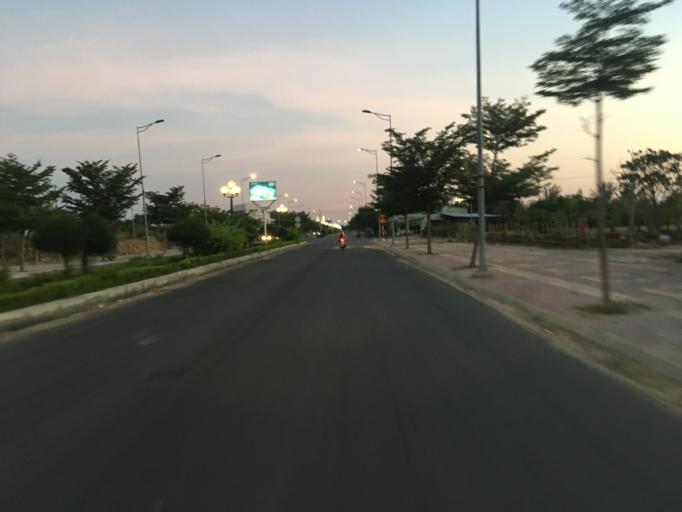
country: VN
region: Ninh Thuan
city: Phan Rang-Thap Cham
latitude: 11.5756
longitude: 109.0012
